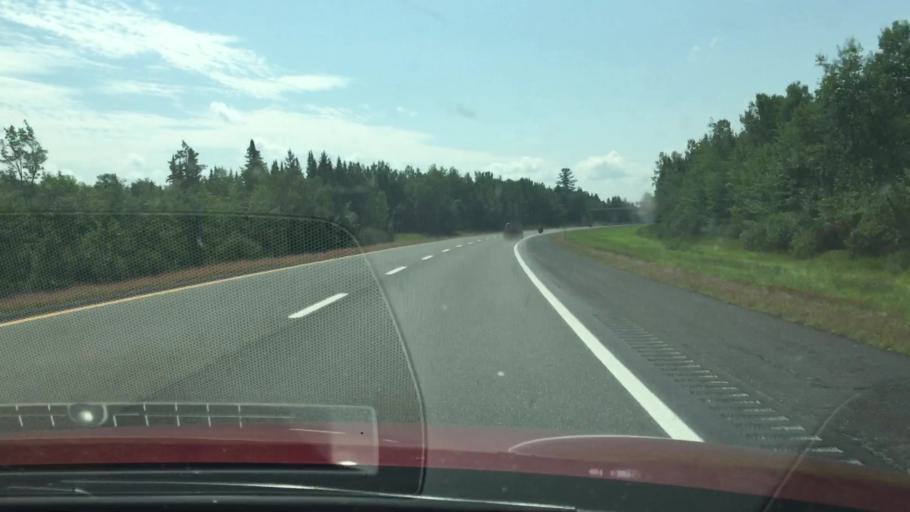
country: US
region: Maine
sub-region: Penobscot County
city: Patten
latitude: 45.9924
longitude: -68.2802
